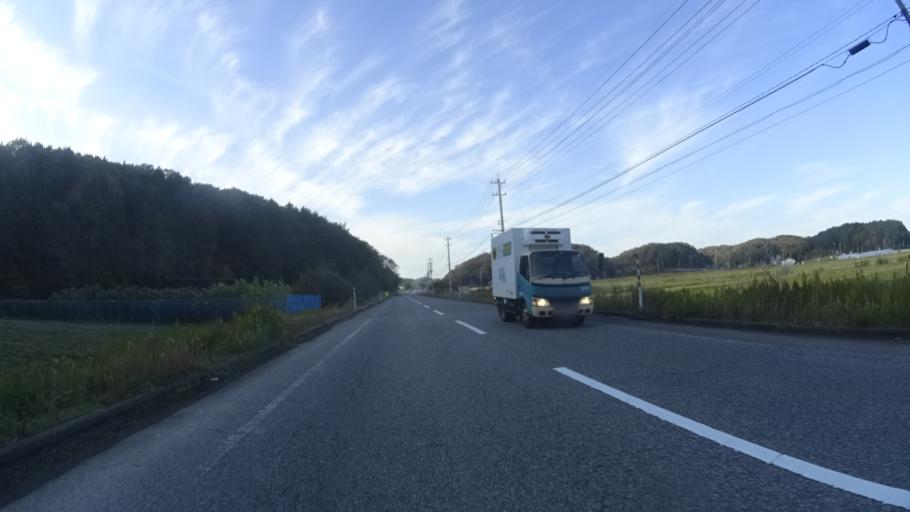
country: JP
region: Ishikawa
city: Hakui
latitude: 37.0180
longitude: 136.7925
